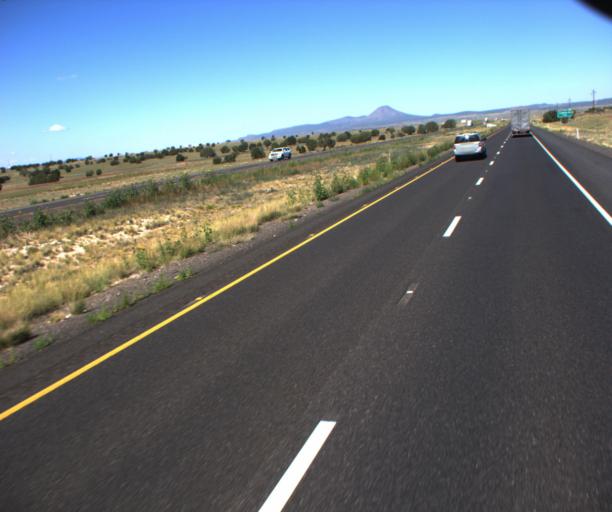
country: US
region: Arizona
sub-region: Yavapai County
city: Paulden
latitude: 35.2251
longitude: -112.5626
